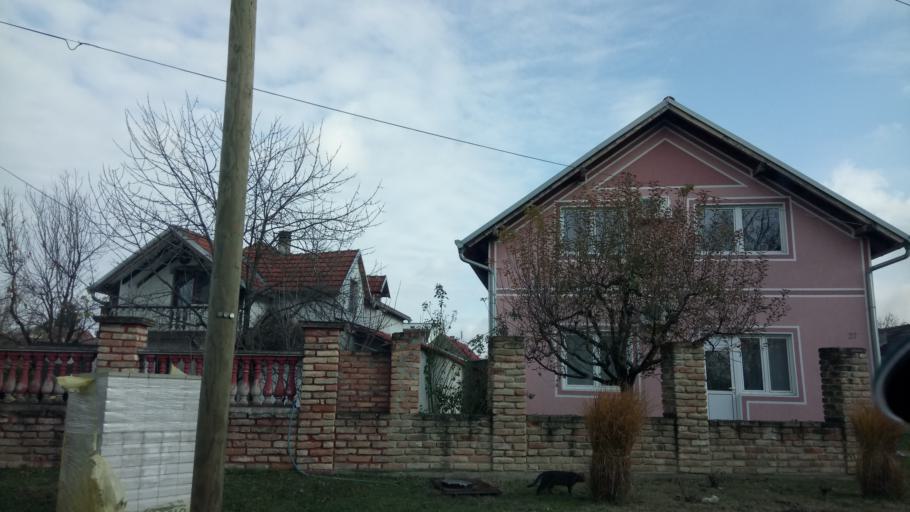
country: RS
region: Autonomna Pokrajina Vojvodina
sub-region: Sremski Okrug
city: Stara Pazova
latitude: 44.9812
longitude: 20.1420
